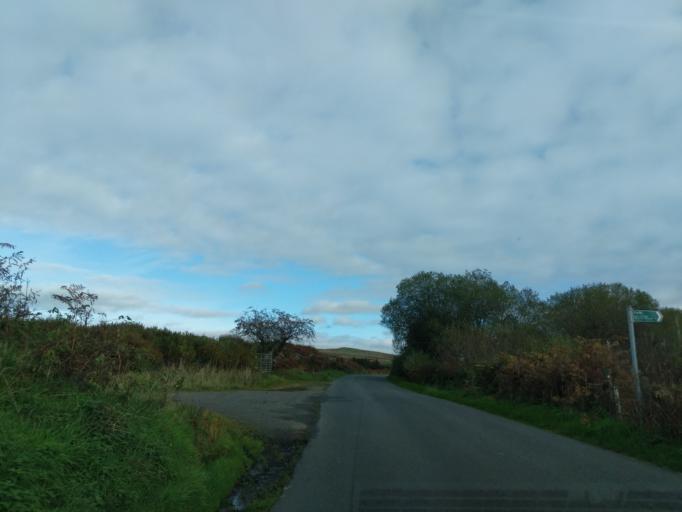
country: GB
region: Scotland
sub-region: Dumfries and Galloway
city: Castle Douglas
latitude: 55.1086
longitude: -4.1119
